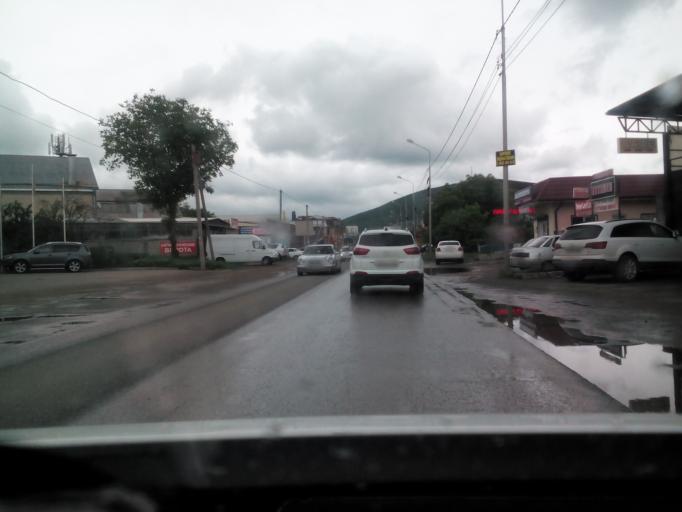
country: RU
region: Stavropol'skiy
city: Pyatigorsk
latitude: 44.0595
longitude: 43.0336
